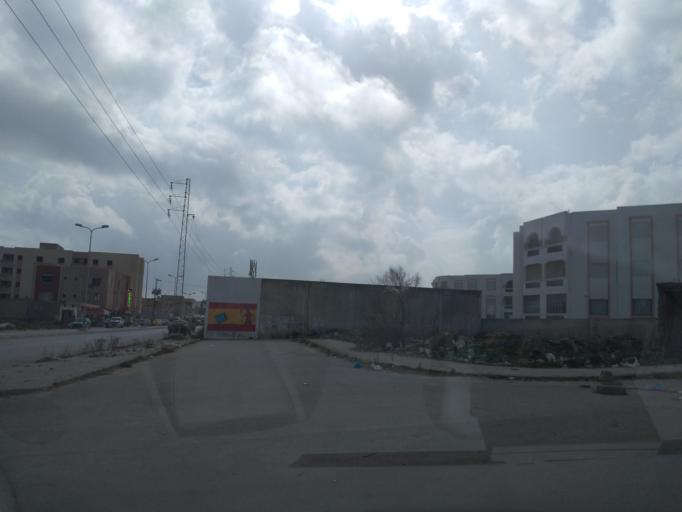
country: TN
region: Ariana
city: Ariana
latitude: 36.9458
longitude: 10.1745
